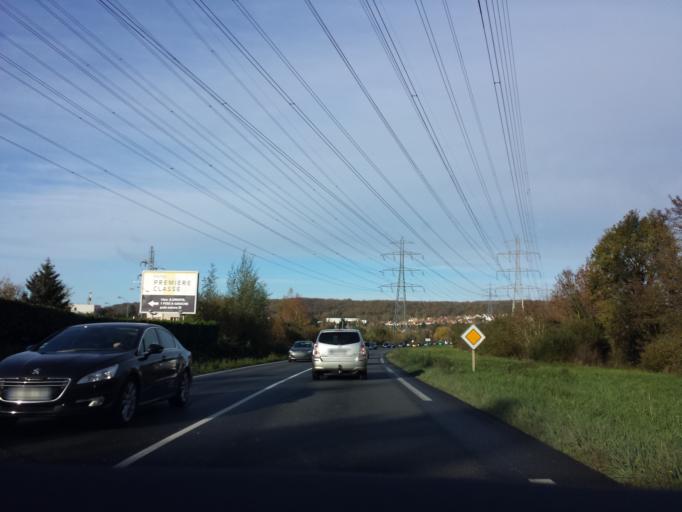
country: FR
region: Ile-de-France
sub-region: Departement de l'Essonne
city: Igny
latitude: 48.7324
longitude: 2.2352
